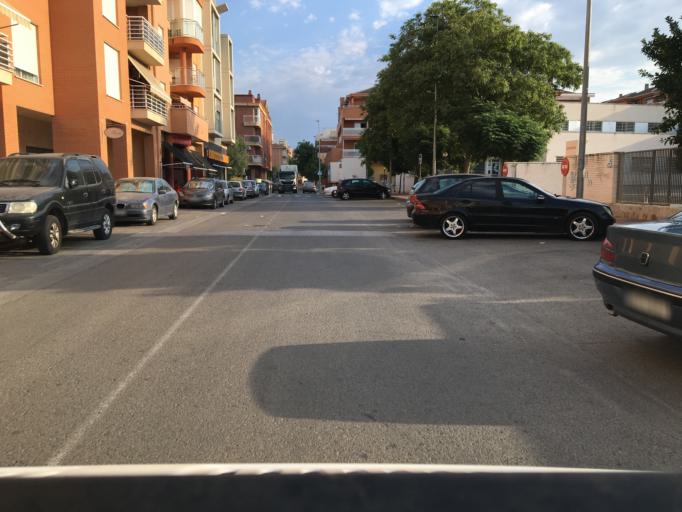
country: ES
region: Murcia
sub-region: Murcia
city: Alcantarilla
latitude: 37.9696
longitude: -1.2066
